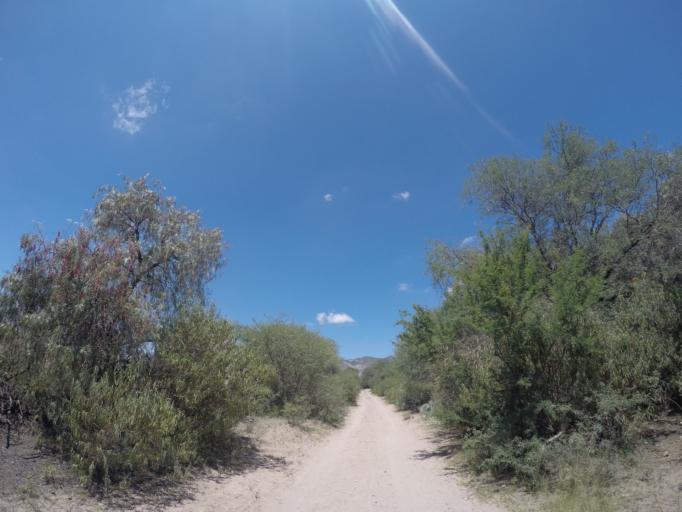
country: MX
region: San Luis Potosi
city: La Pila
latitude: 21.9823
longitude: -100.8965
